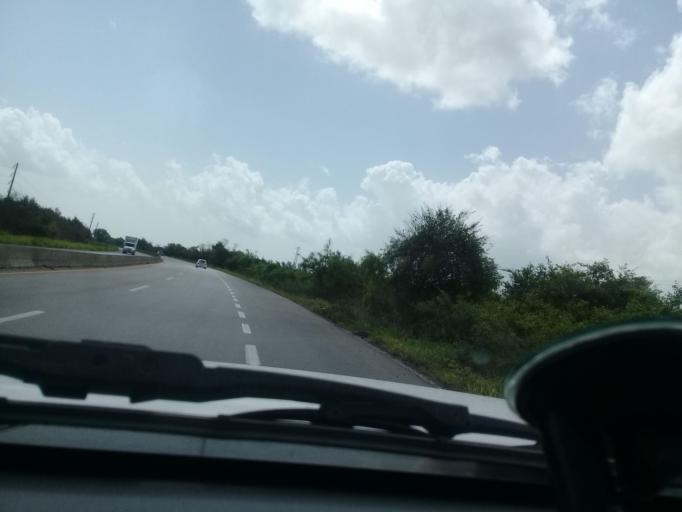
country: MX
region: Veracruz
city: Moralillo
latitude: 22.2117
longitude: -97.9633
